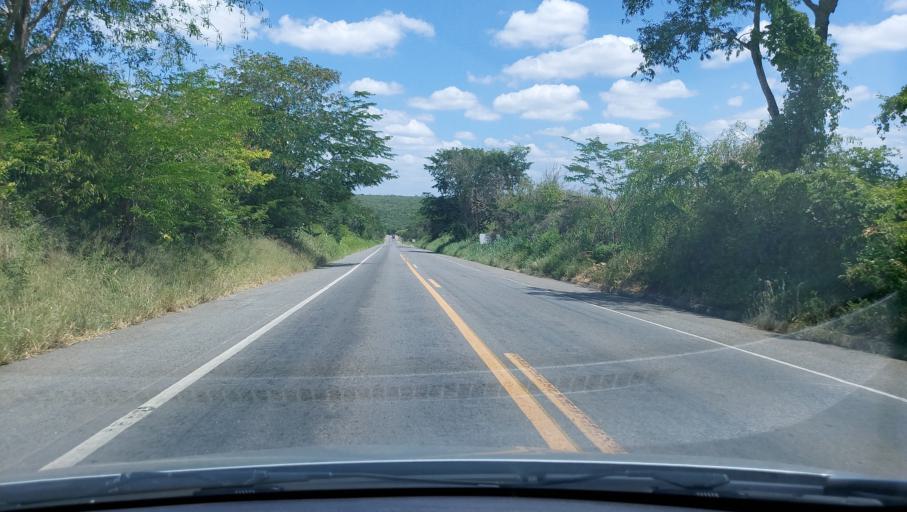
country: BR
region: Bahia
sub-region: Andarai
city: Vera Cruz
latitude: -12.5046
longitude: -41.2188
